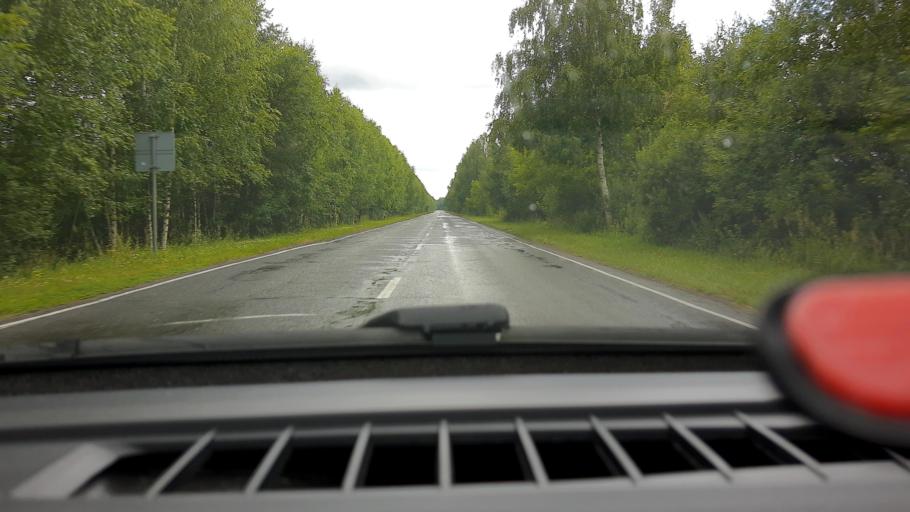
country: RU
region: Nizjnij Novgorod
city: Neklyudovo
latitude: 56.5135
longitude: 43.9407
